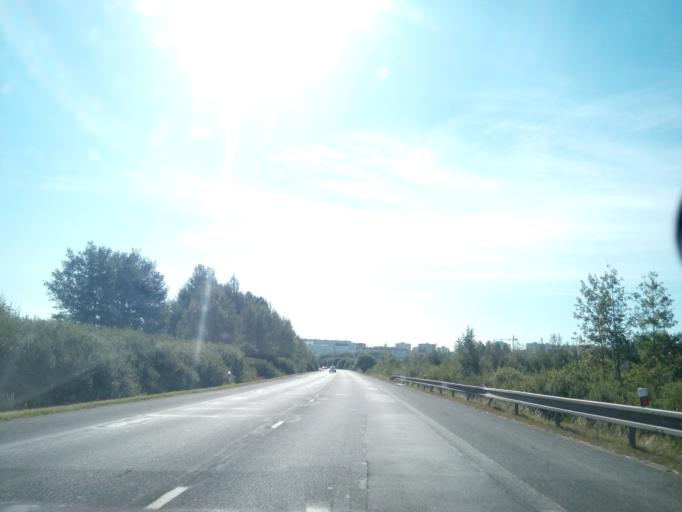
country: SK
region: Presovsky
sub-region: Okres Poprad
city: Poprad
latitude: 49.0521
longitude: 20.2810
